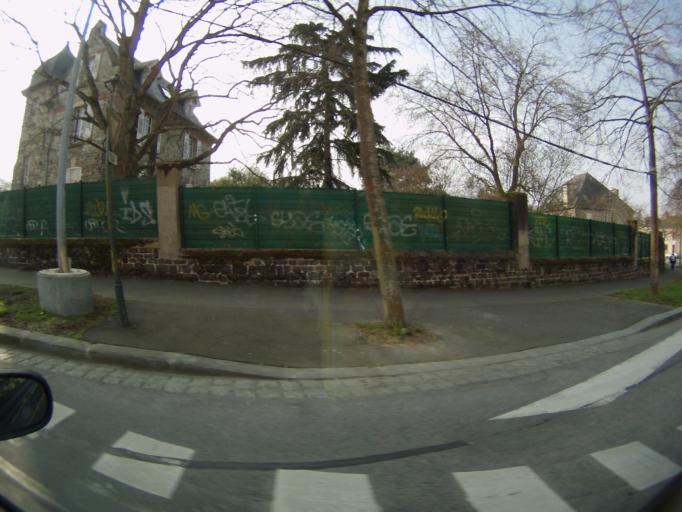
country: FR
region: Brittany
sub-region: Departement d'Ille-et-Vilaine
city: Rennes
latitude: 48.1146
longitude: -1.6562
